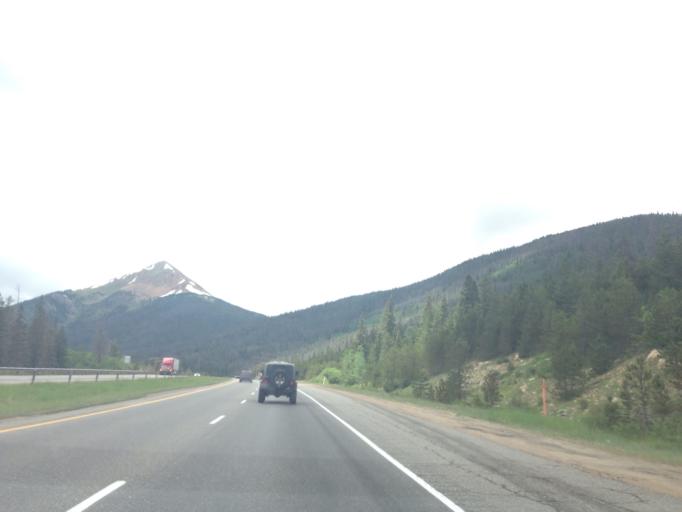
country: US
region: Colorado
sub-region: Clear Creek County
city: Georgetown
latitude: 39.6989
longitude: -105.8336
